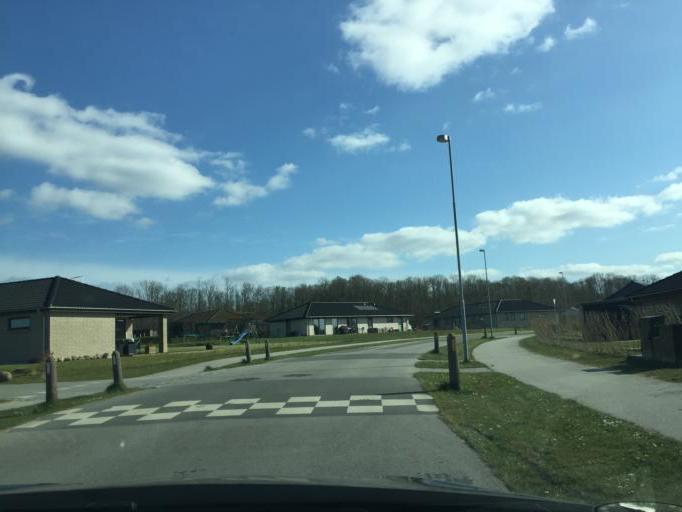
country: DK
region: South Denmark
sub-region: Faaborg-Midtfyn Kommune
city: Arslev
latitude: 55.3046
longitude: 10.4974
